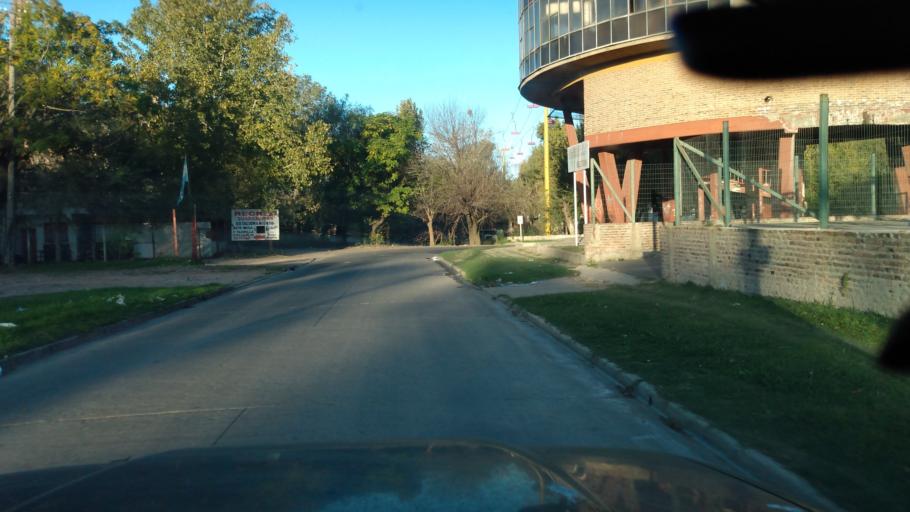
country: AR
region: Buenos Aires
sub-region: Partido de Lujan
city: Lujan
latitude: -34.5648
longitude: -59.1246
